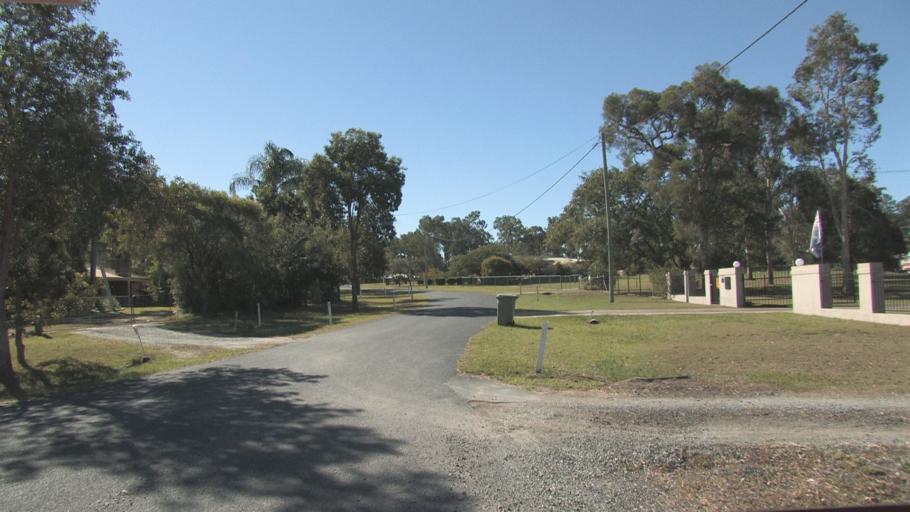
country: AU
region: Queensland
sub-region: Logan
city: Park Ridge South
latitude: -27.7299
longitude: 153.0531
